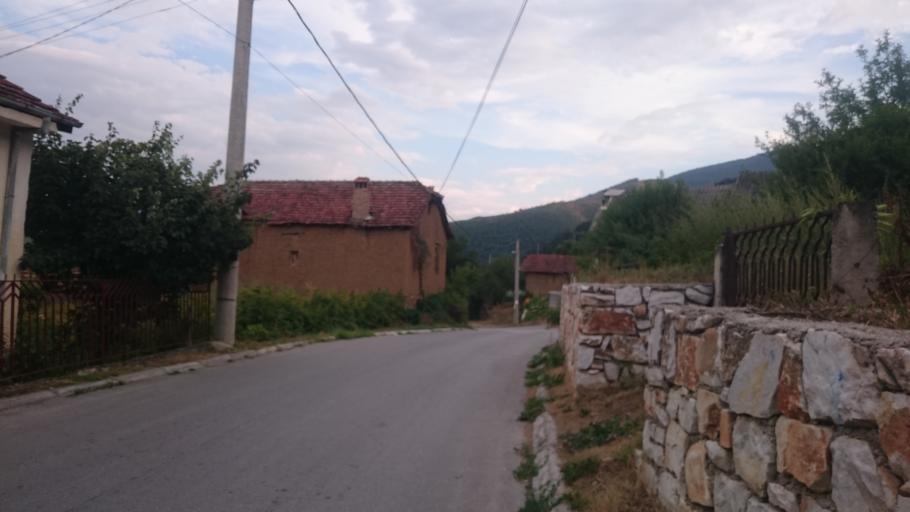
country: MK
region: Makedonski Brod
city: Makedonski Brod
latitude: 41.5148
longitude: 21.2132
